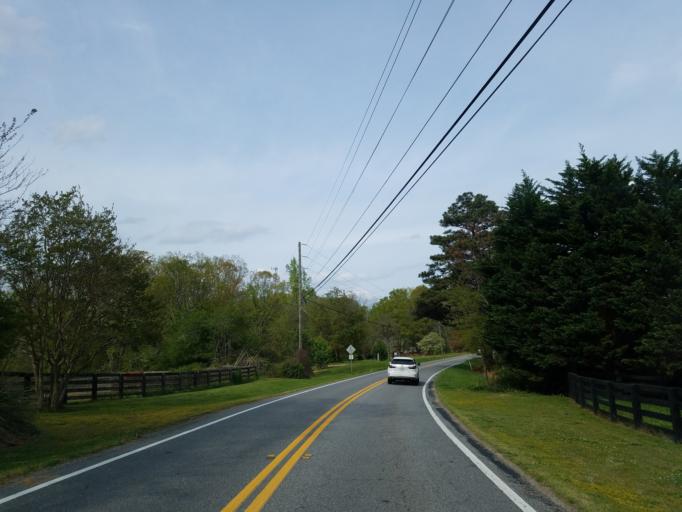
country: US
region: Georgia
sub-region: Fulton County
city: Johns Creek
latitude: 34.1080
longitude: -84.1946
